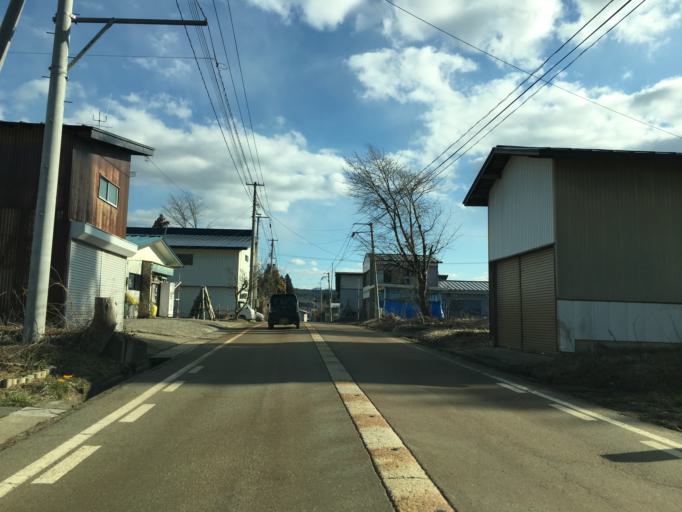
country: JP
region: Yamagata
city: Yonezawa
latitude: 37.9618
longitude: 139.9891
